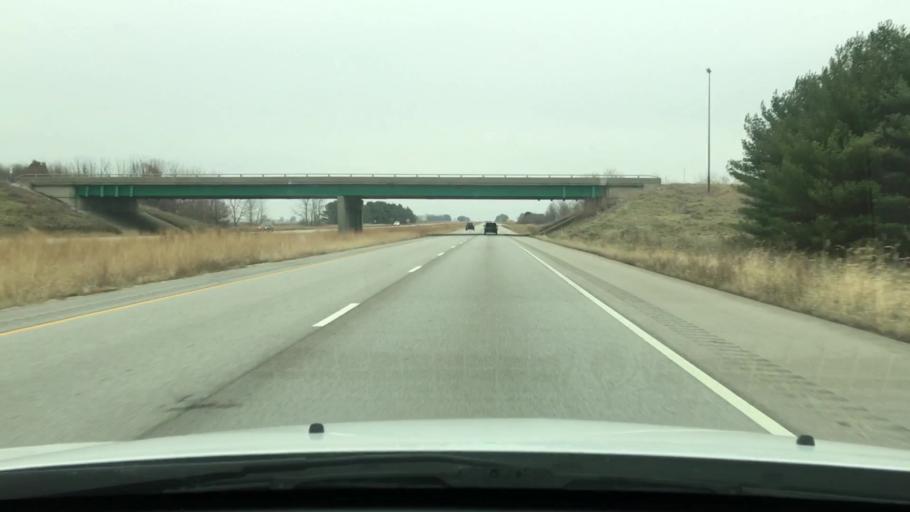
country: US
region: Illinois
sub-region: Sangamon County
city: New Berlin
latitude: 39.7368
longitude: -90.0431
